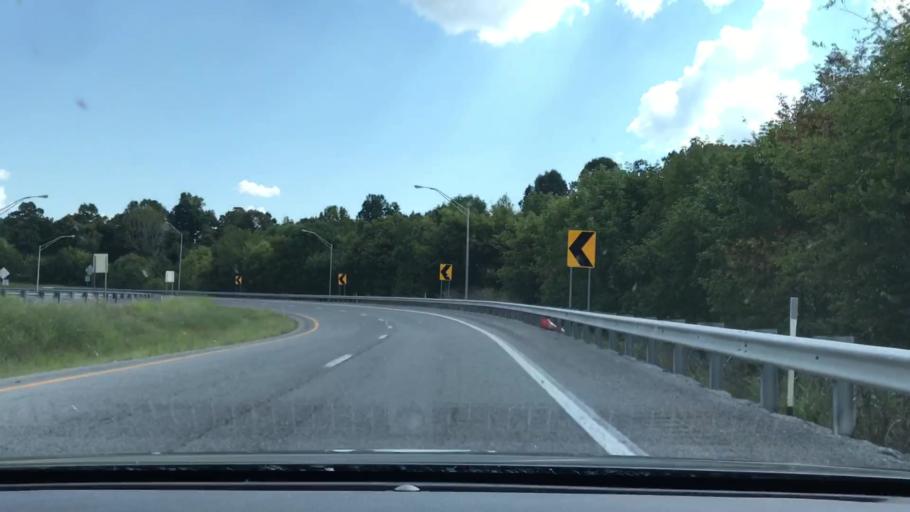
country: US
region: Kentucky
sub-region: Lyon County
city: Eddyville
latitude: 37.0709
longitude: -88.0892
